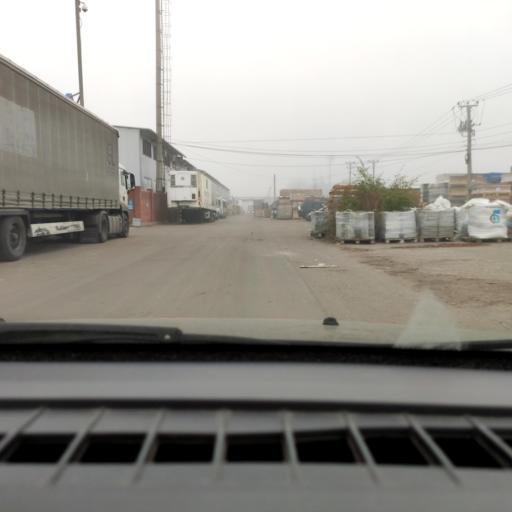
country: RU
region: Samara
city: Tol'yatti
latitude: 53.5734
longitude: 49.2832
